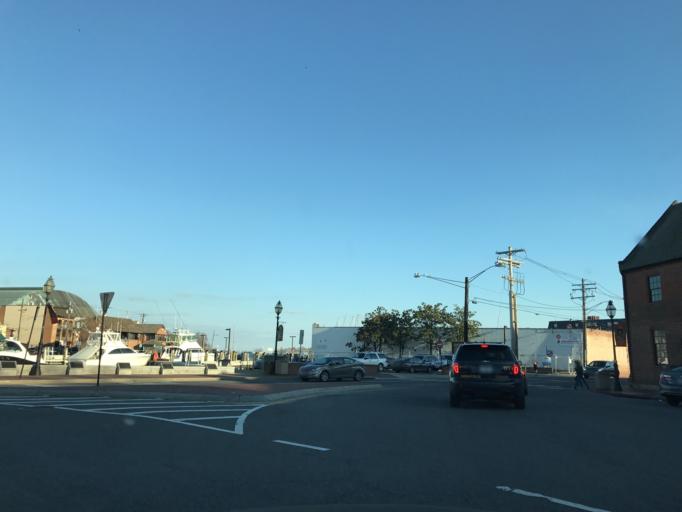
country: US
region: Maryland
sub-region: Anne Arundel County
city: Annapolis
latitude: 38.9774
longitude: -76.4873
